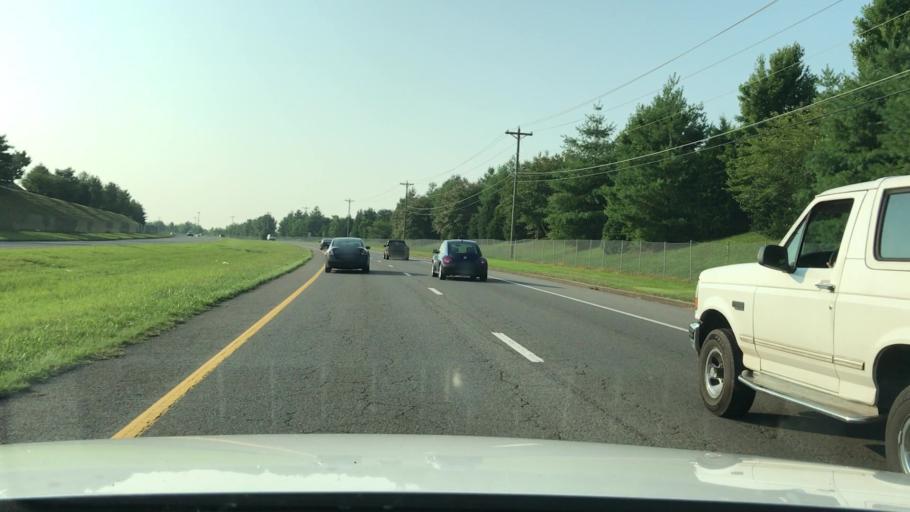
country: US
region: Tennessee
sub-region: Sumner County
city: Gallatin
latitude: 36.3673
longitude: -86.4589
